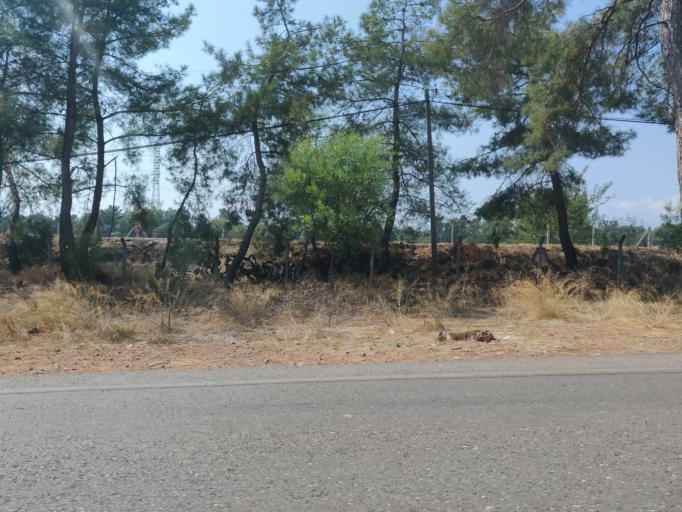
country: TR
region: Antalya
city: Dosemealti
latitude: 36.9536
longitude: 30.6300
